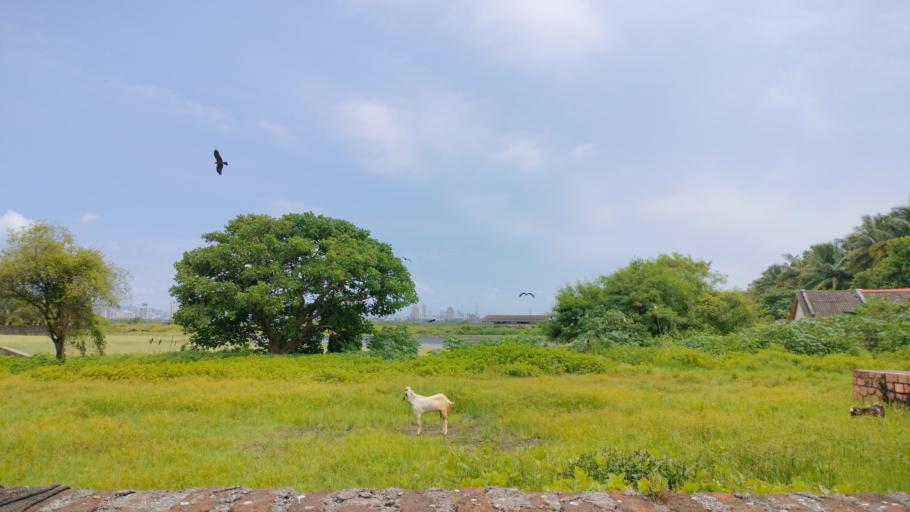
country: IN
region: Maharashtra
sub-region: Mumbai Suburban
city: Borivli
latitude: 19.2083
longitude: 72.7852
